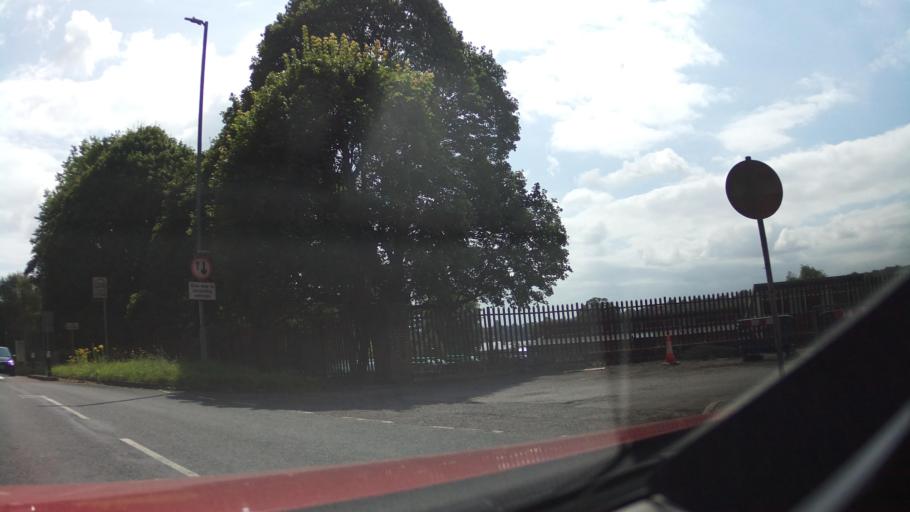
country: GB
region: England
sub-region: Dorset
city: Blandford Forum
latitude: 50.8655
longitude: -2.1709
